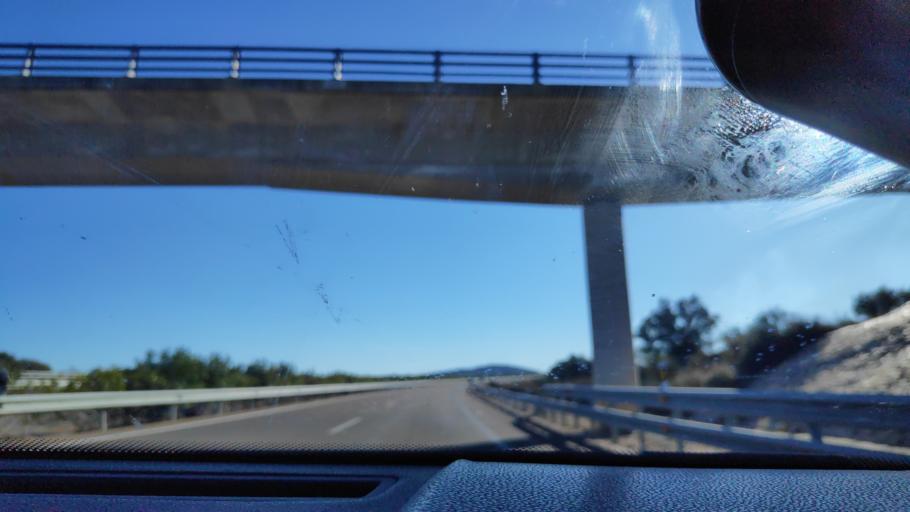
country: ES
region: Extremadura
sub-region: Provincia de Badajoz
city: Los Santos de Maimona
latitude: 38.4919
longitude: -6.3551
